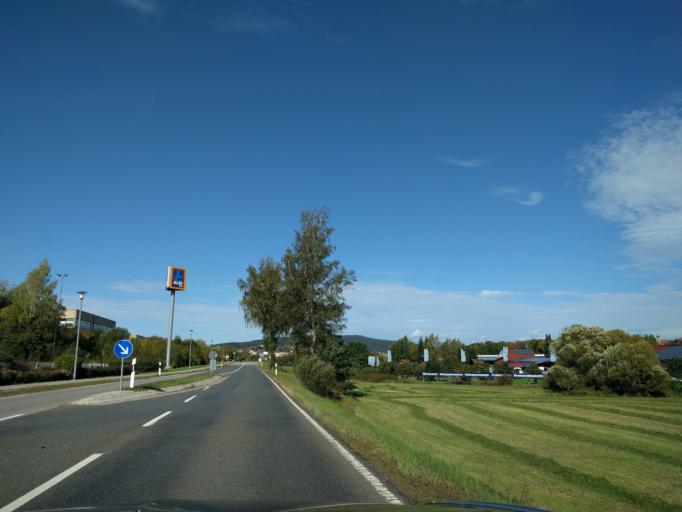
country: DE
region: Bavaria
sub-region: Upper Palatinate
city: Kotzting
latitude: 49.1669
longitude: 12.8723
